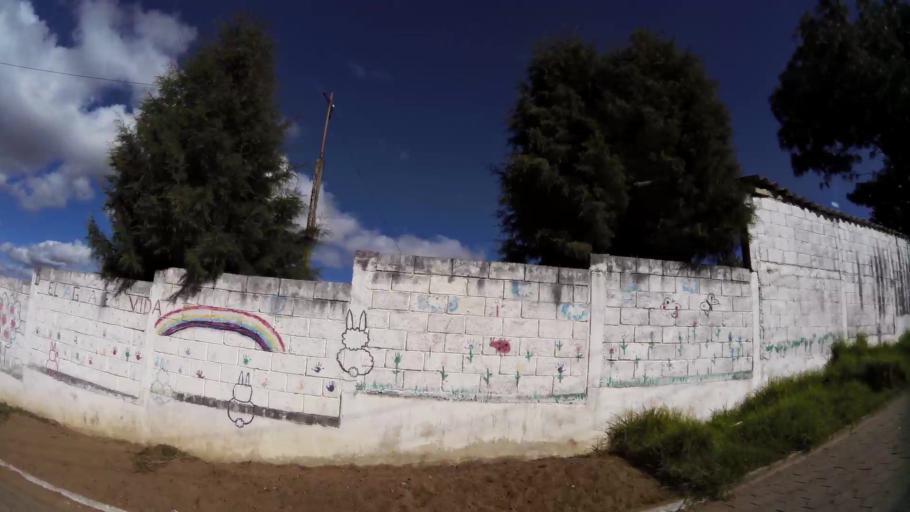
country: GT
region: Quetzaltenango
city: Quetzaltenango
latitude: 14.8345
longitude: -91.5045
